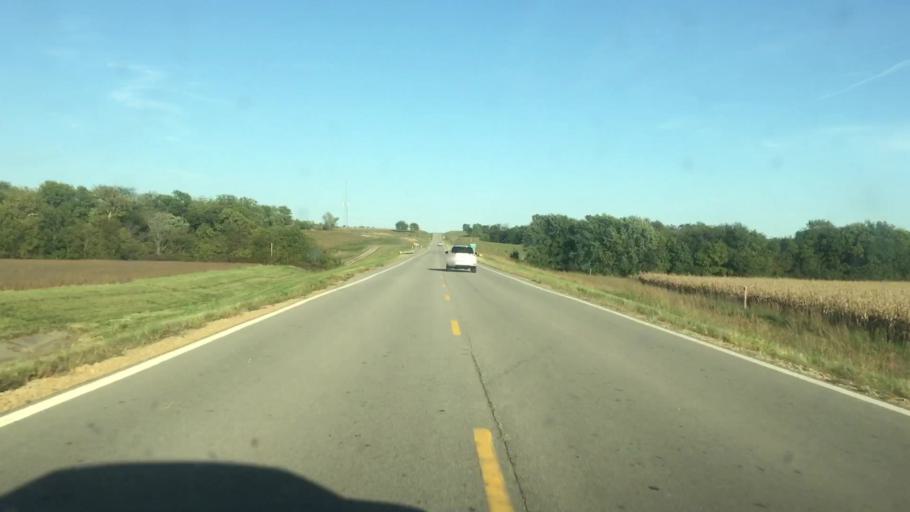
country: US
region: Kansas
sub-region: Brown County
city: Horton
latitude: 39.5875
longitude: -95.5583
